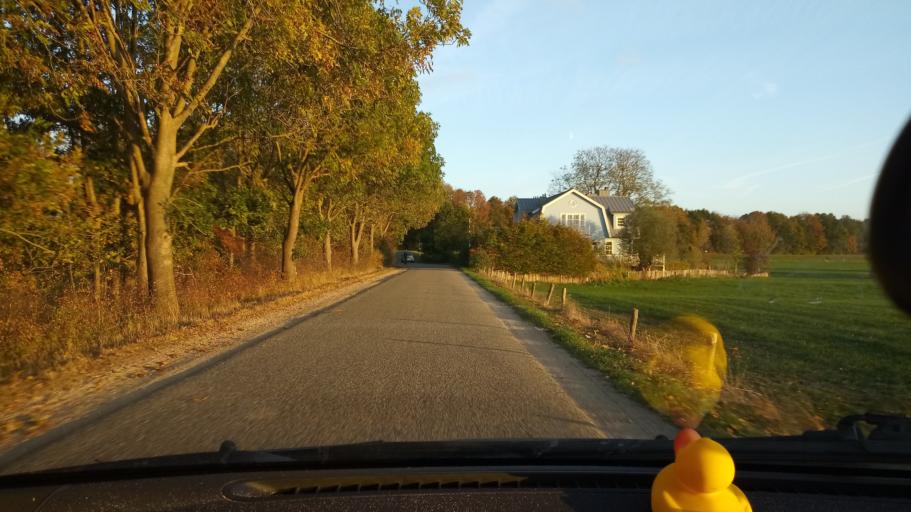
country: NL
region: Gelderland
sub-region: Gemeente Zutphen
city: Zutphen
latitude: 52.1565
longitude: 6.1767
